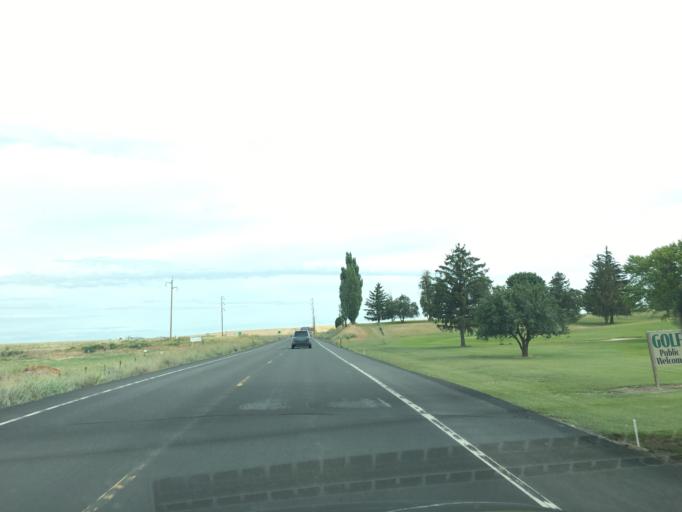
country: US
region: Washington
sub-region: Okanogan County
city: Coulee Dam
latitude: 47.7664
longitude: -118.7220
